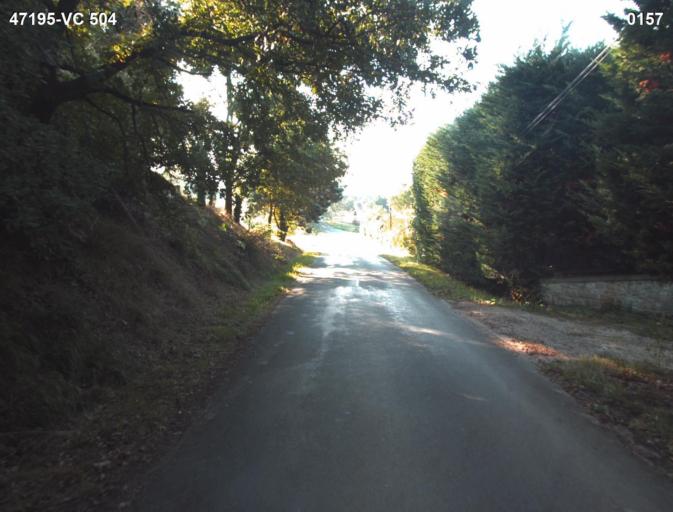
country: FR
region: Aquitaine
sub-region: Departement du Lot-et-Garonne
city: Nerac
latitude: 44.1495
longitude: 0.3367
